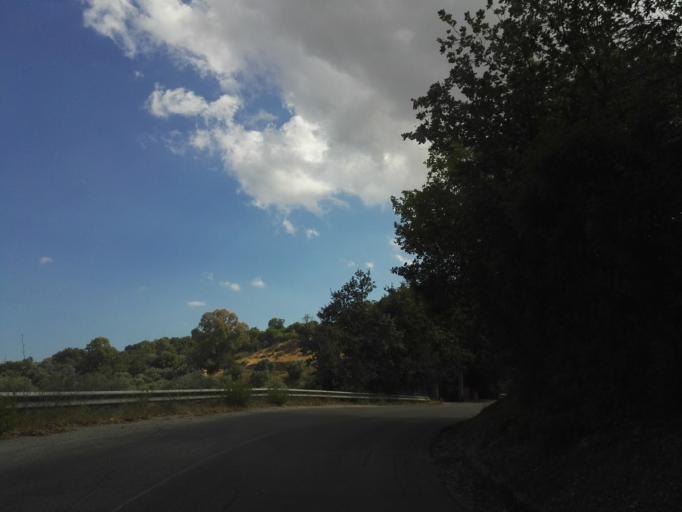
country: IT
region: Calabria
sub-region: Provincia di Reggio Calabria
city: Camini
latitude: 38.4276
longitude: 16.4868
